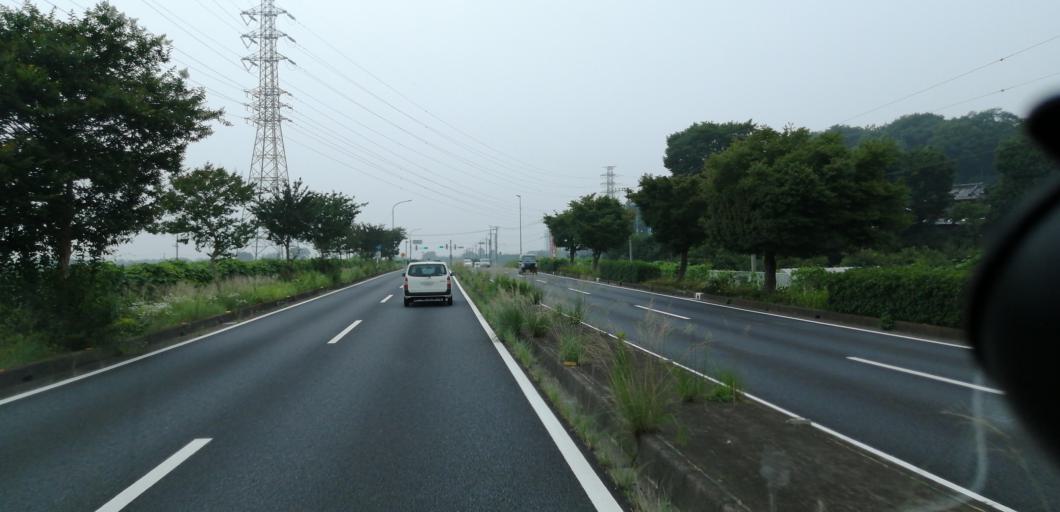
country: JP
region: Saitama
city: Fukayacho
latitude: 36.1508
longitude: 139.3159
